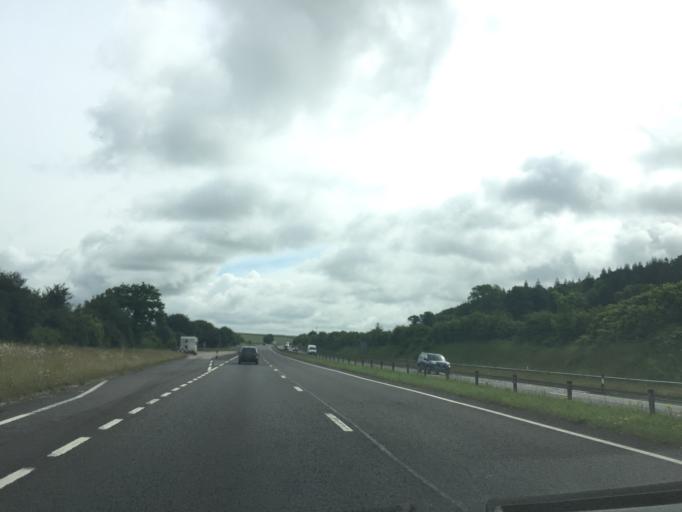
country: GB
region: England
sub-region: Dorset
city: Bovington Camp
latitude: 50.7544
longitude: -2.2465
